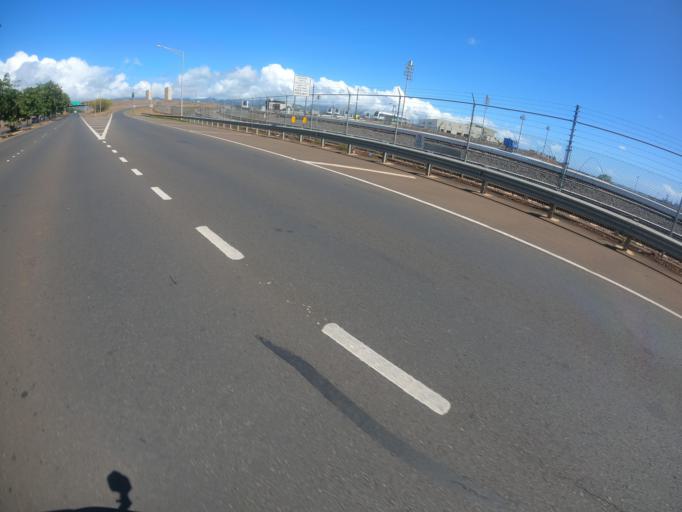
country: US
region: Hawaii
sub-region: Honolulu County
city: Pearl City, Manana
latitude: 21.3923
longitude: -157.9915
